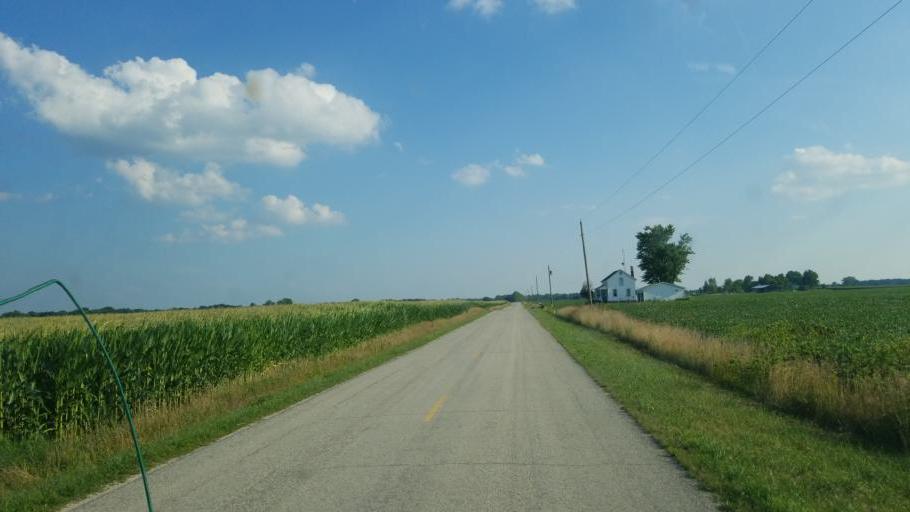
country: US
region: Ohio
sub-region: Crawford County
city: Bucyrus
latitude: 40.8491
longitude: -82.9018
